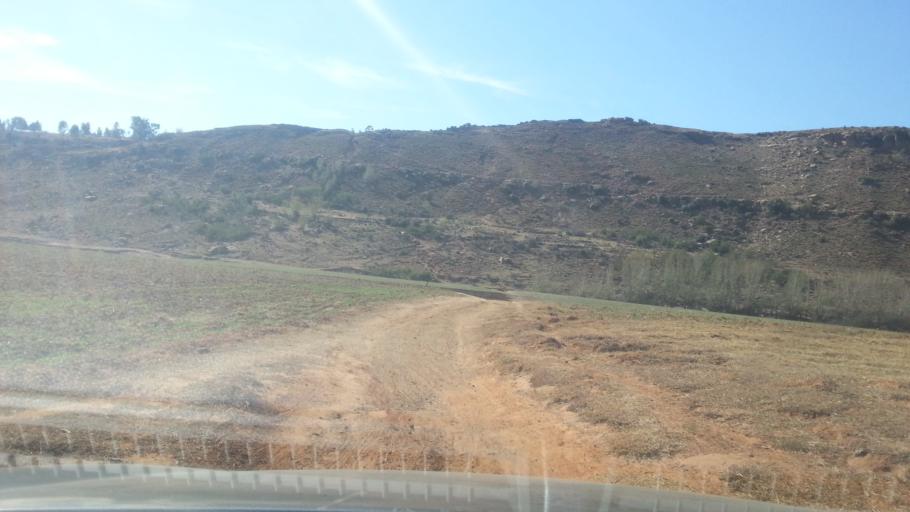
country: LS
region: Maseru
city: Nako
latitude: -29.4805
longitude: 27.6432
